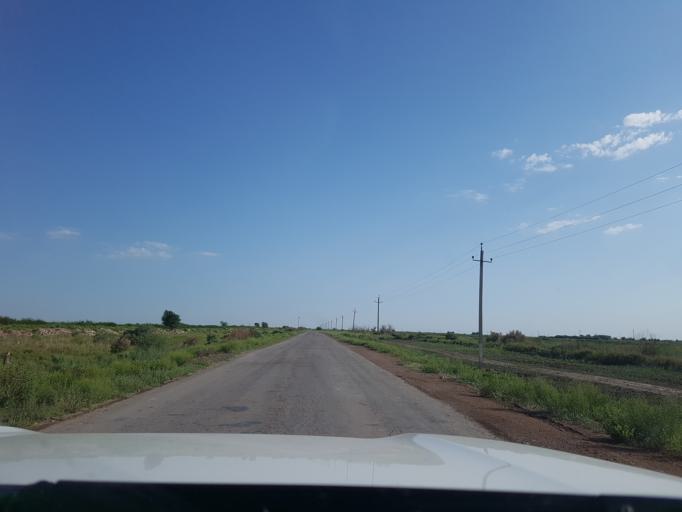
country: TM
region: Dasoguz
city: Koeneuergench
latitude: 41.8702
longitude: 58.7059
